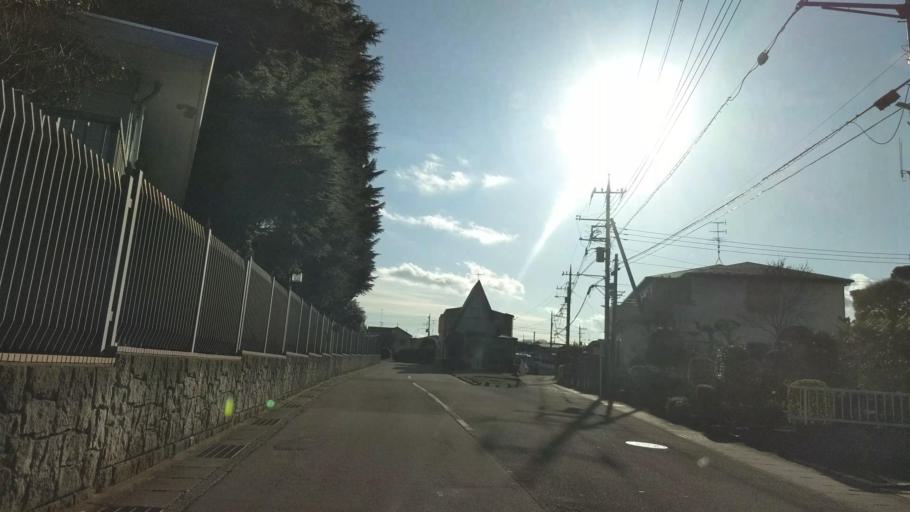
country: JP
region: Kanagawa
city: Isehara
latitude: 35.3623
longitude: 139.2710
